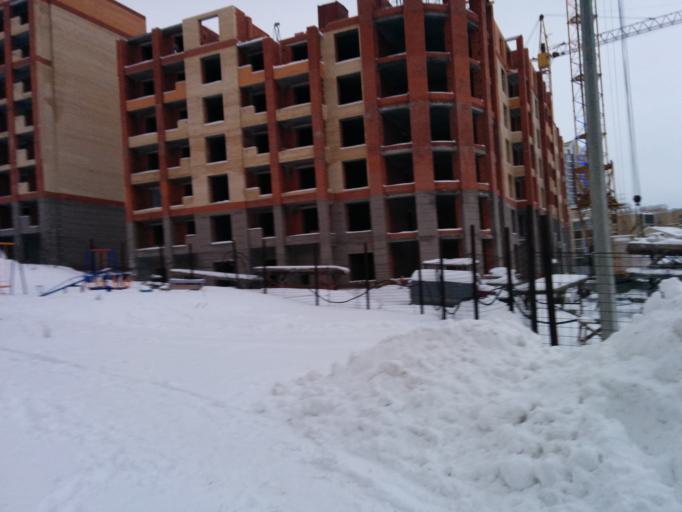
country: RU
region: Chuvashia
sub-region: Cheboksarskiy Rayon
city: Cheboksary
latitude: 56.1406
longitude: 47.2315
